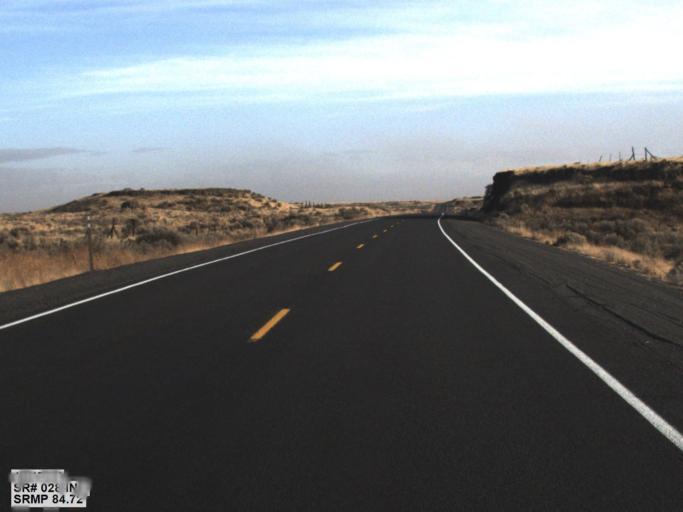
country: US
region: Washington
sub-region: Grant County
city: Warden
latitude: 47.3273
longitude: -118.8722
